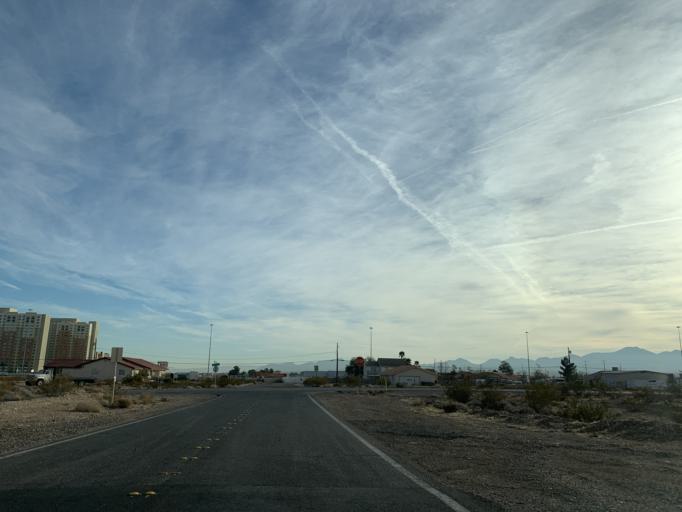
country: US
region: Nevada
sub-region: Clark County
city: Enterprise
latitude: 36.0063
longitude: -115.1841
